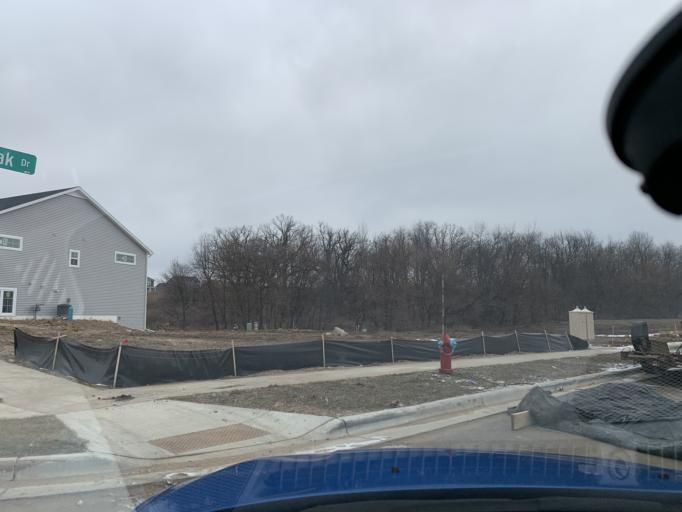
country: US
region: Wisconsin
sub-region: Dane County
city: Middleton
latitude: 43.0685
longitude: -89.5657
